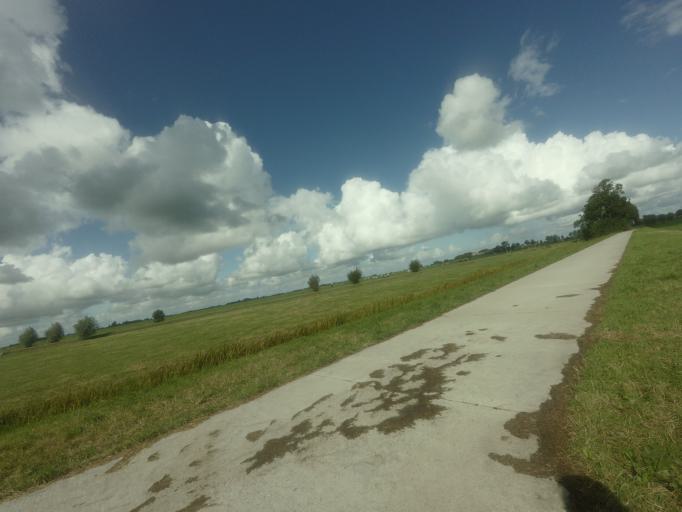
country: NL
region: Friesland
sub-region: Gemeente Littenseradiel
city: Makkum
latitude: 53.0899
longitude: 5.7040
